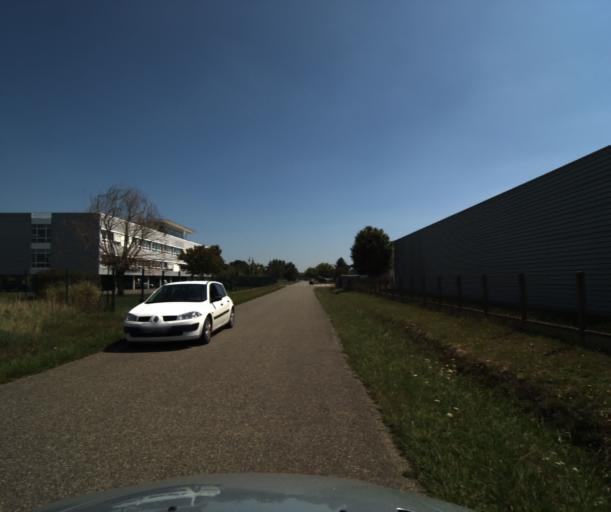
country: FR
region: Midi-Pyrenees
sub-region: Departement de la Haute-Garonne
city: Labastidette
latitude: 43.4506
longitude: 1.2681
